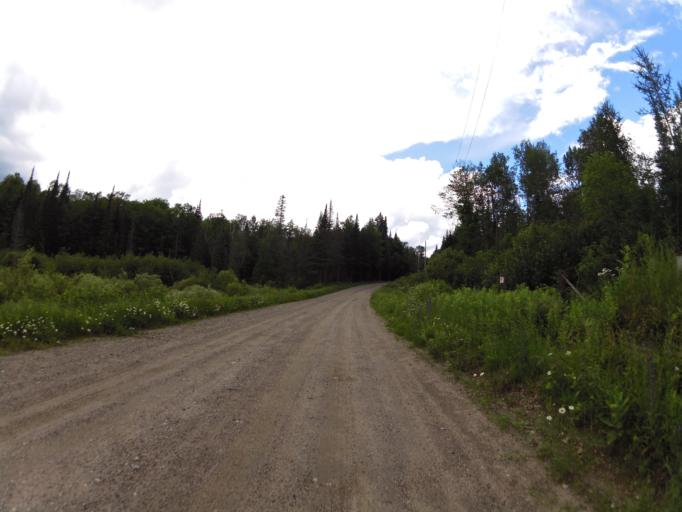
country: CA
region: Ontario
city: Renfrew
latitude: 45.0618
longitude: -76.7546
